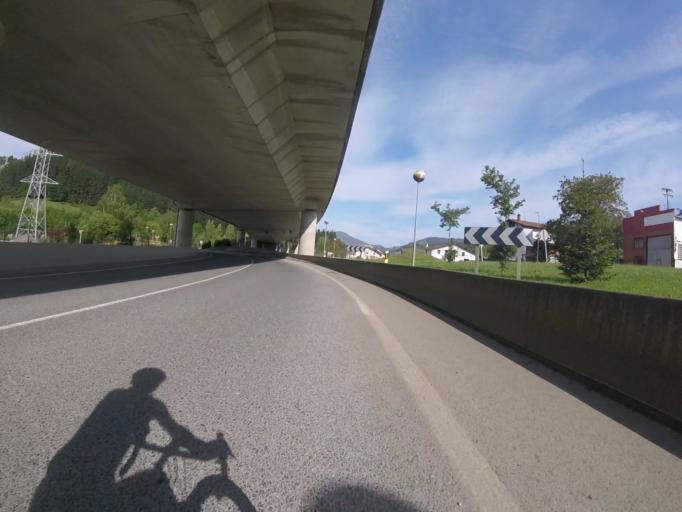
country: ES
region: Basque Country
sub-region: Provincia de Guipuzcoa
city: Gabiria
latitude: 43.0629
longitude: -2.2743
